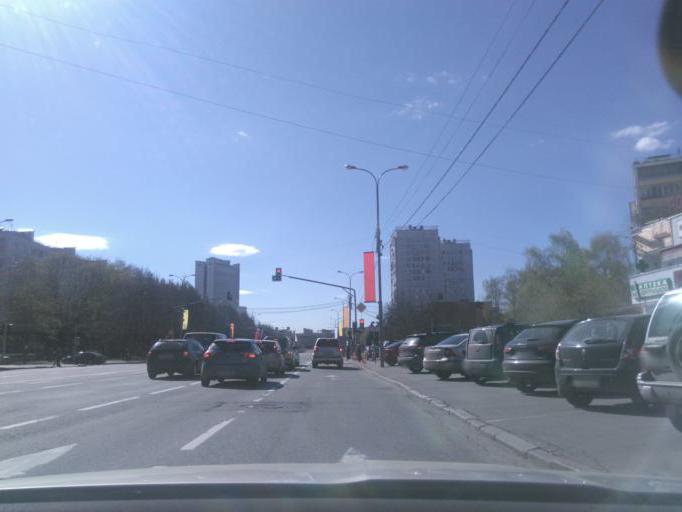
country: RU
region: Moscow
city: Zelenograd
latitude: 55.9962
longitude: 37.2121
